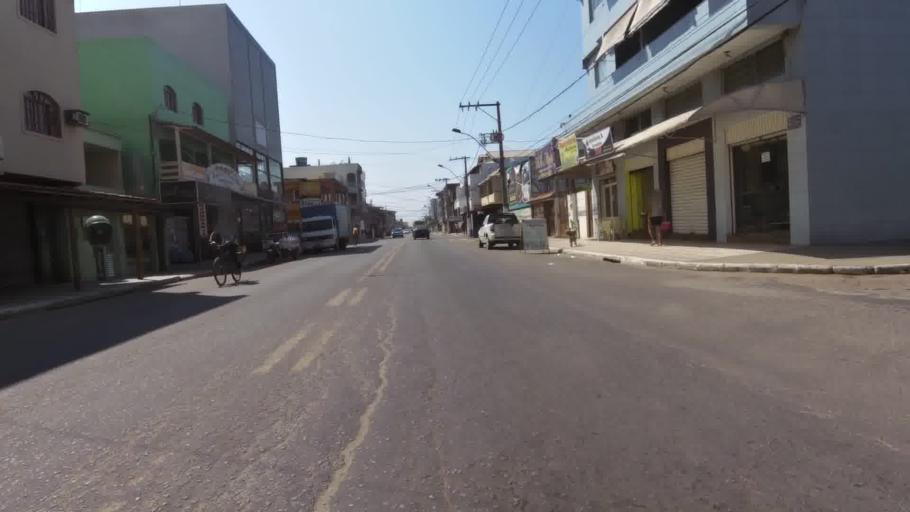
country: BR
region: Espirito Santo
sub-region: Marataizes
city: Marataizes
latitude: -21.0317
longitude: -40.8178
